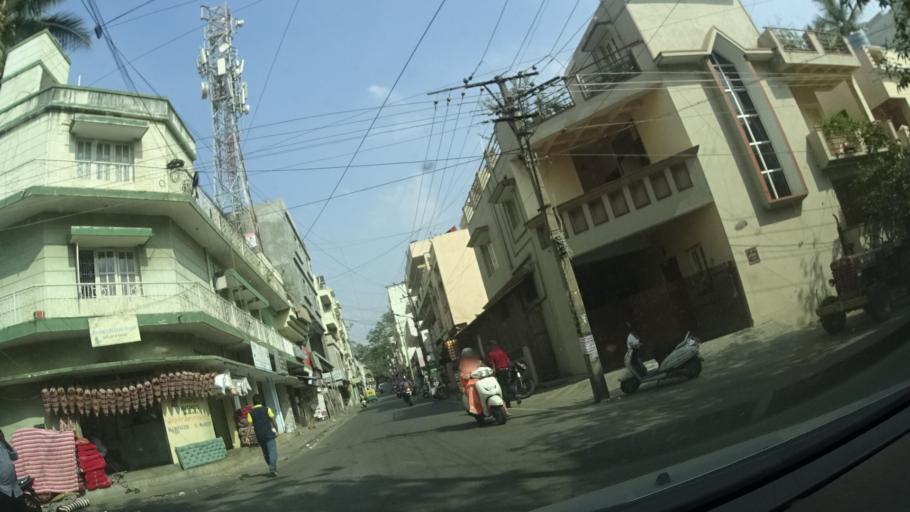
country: IN
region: Karnataka
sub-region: Bangalore Urban
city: Bangalore
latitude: 12.9447
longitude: 77.5598
